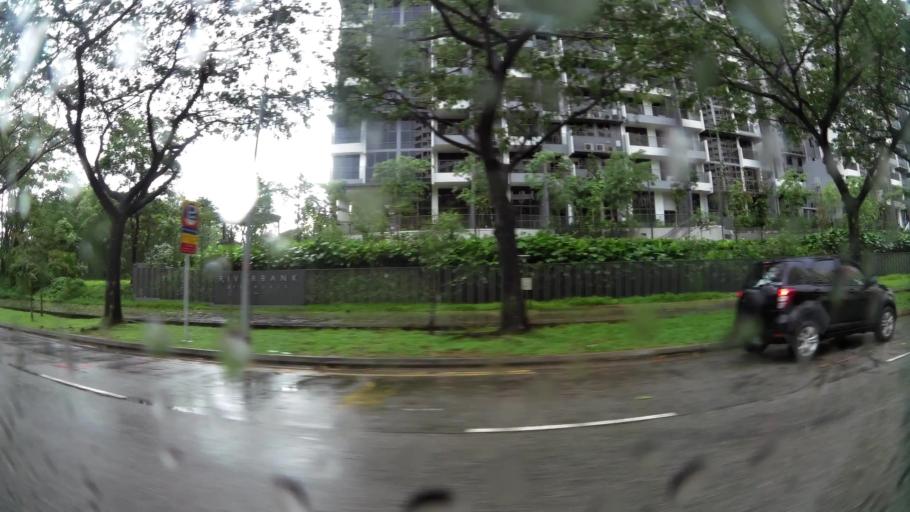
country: MY
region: Johor
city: Kampung Pasir Gudang Baru
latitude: 1.3954
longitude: 103.8816
